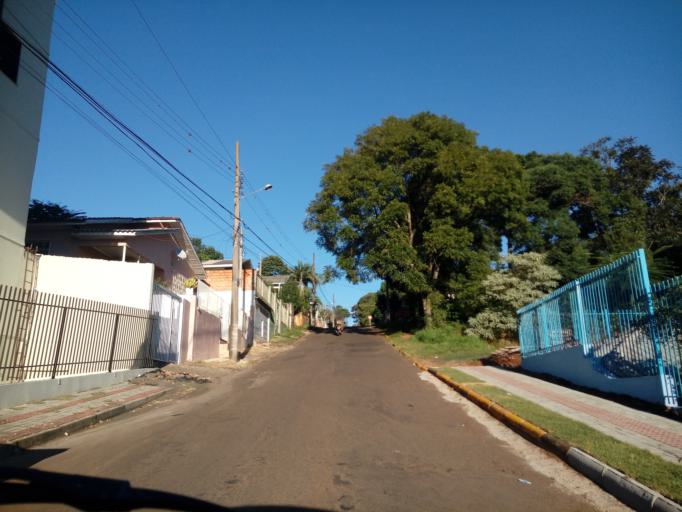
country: BR
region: Santa Catarina
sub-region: Chapeco
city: Chapeco
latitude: -27.1129
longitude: -52.6071
